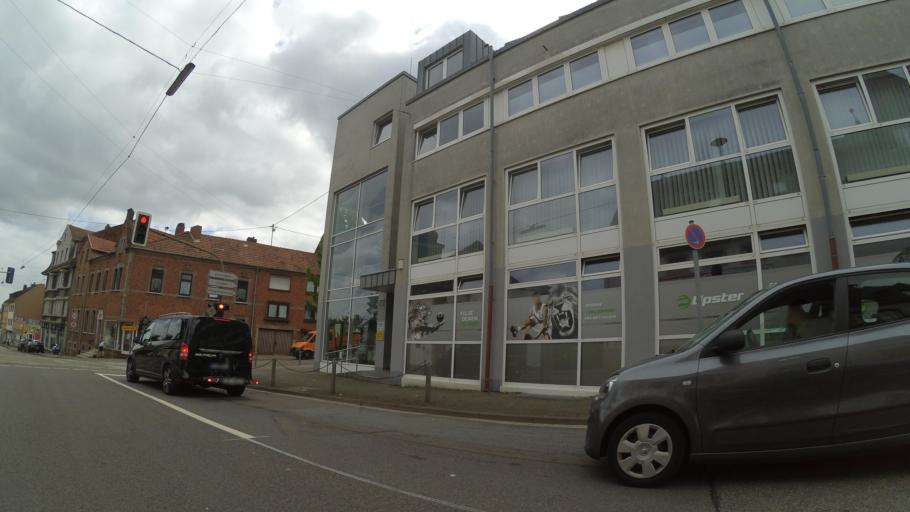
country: FR
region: Lorraine
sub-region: Departement de la Moselle
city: Schoeneck
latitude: 49.2368
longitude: 6.9289
